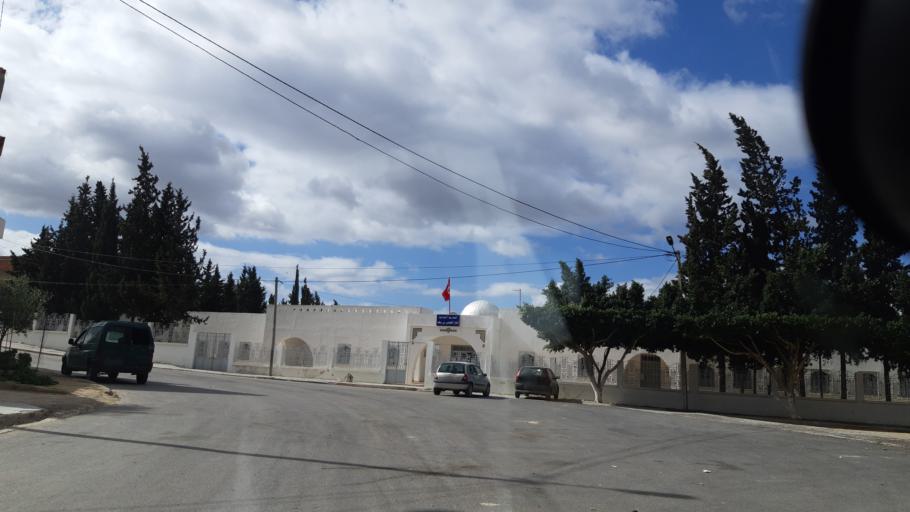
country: TN
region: Susah
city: Akouda
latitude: 35.8715
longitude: 10.5184
